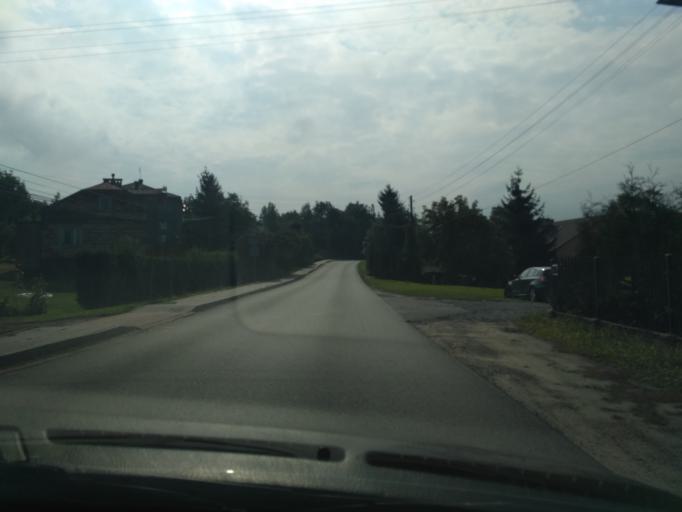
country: PL
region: Subcarpathian Voivodeship
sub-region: Powiat rzeszowski
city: Kielanowka
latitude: 50.0072
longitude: 21.9077
